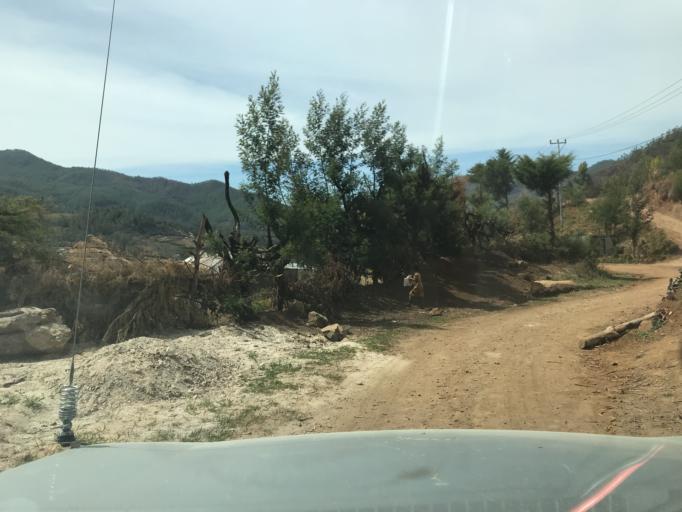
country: TL
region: Ainaro
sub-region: Ainaro
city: Ainaro
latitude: -8.8878
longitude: 125.5194
